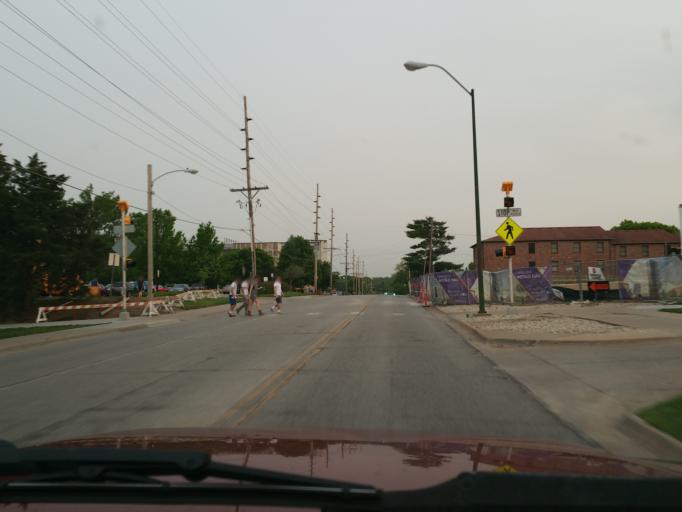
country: US
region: Kansas
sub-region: Riley County
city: Manhattan
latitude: 39.1923
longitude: -96.5855
